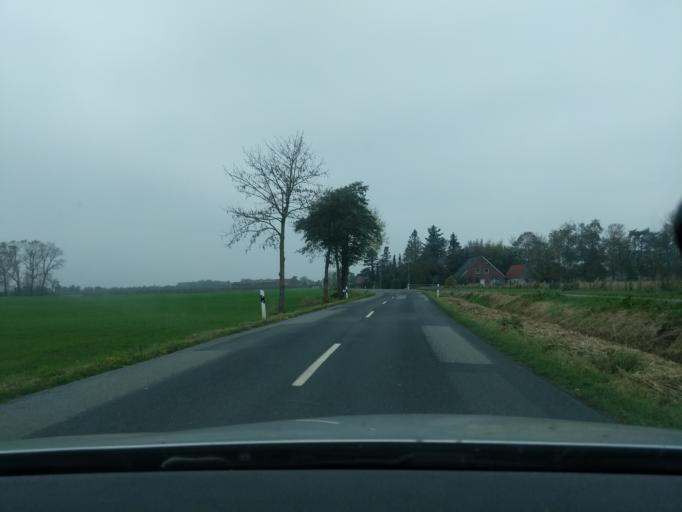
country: DE
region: Lower Saxony
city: Otterndorf
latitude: 53.8198
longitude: 8.8615
